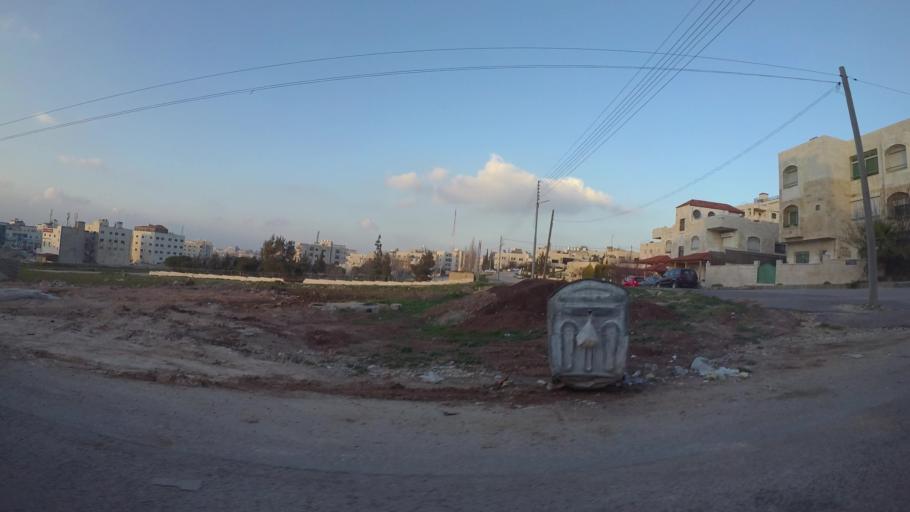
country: JO
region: Amman
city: Al Quwaysimah
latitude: 31.8975
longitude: 35.9262
